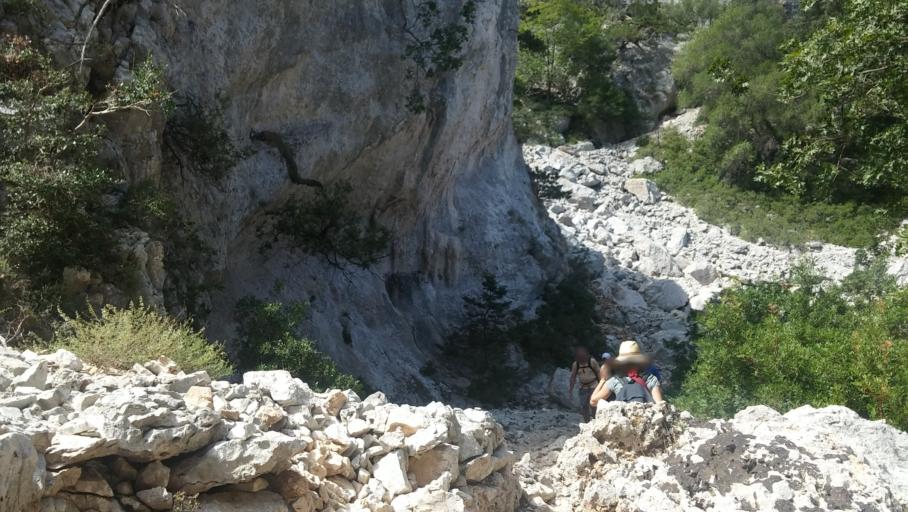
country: IT
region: Sardinia
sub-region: Provincia di Ogliastra
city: Baunei
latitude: 40.1033
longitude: 9.6870
